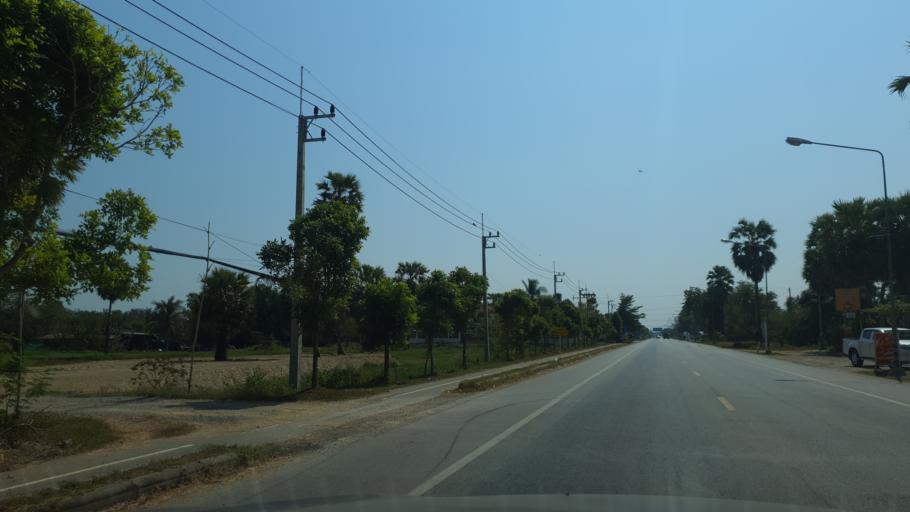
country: TH
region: Prachuap Khiri Khan
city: Pran Buri
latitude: 12.3643
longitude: 99.9346
